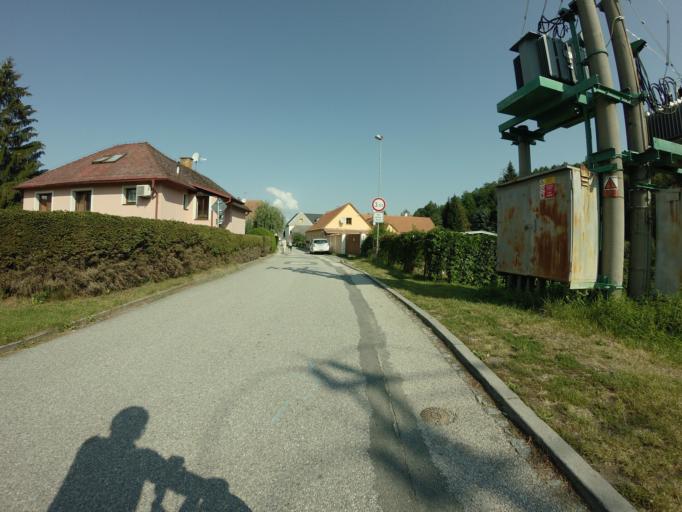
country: CZ
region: Jihocesky
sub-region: Okres Cesky Krumlov
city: Vyssi Brod
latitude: 48.6196
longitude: 14.3127
